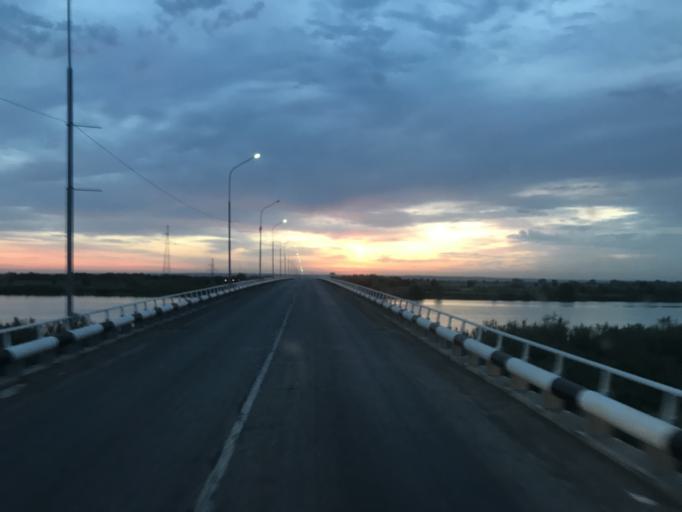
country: KZ
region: Ongtustik Qazaqstan
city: Ilyich
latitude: 41.0286
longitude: 68.5161
